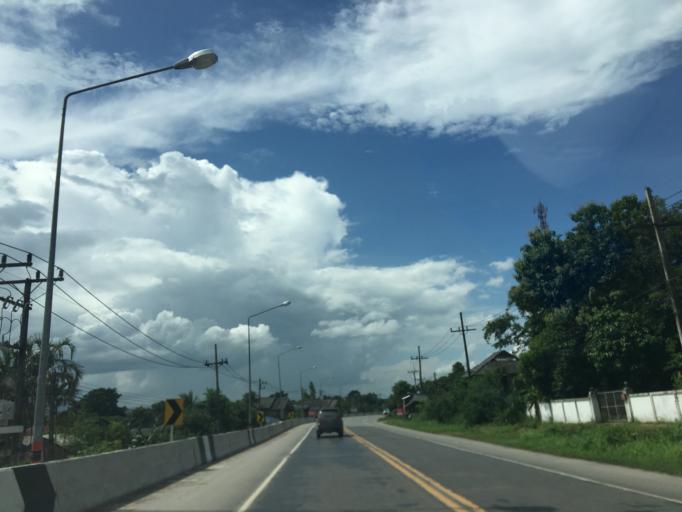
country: TH
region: Chiang Rai
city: Pa Daet
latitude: 19.6560
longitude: 99.9335
